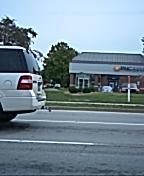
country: US
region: Kentucky
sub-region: Jefferson County
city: Hurstbourne Acres
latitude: 38.2285
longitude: -85.5774
